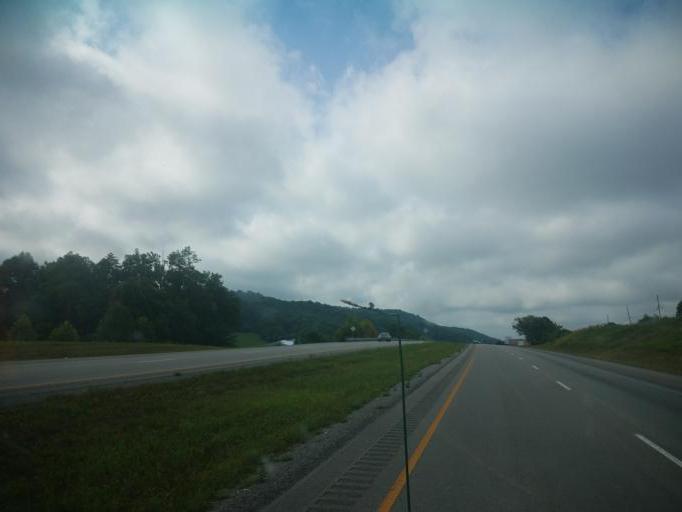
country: US
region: Kentucky
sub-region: Clinton County
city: Albany
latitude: 36.7462
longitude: -85.1358
